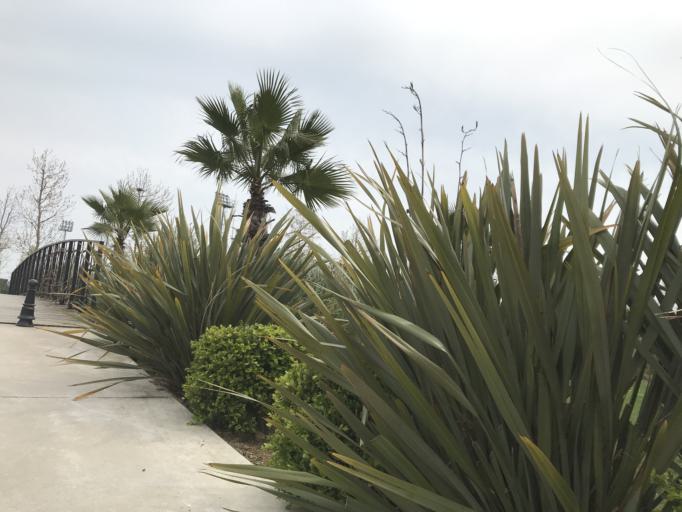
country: TR
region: Istanbul
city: Maltepe
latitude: 40.9382
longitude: 29.1101
